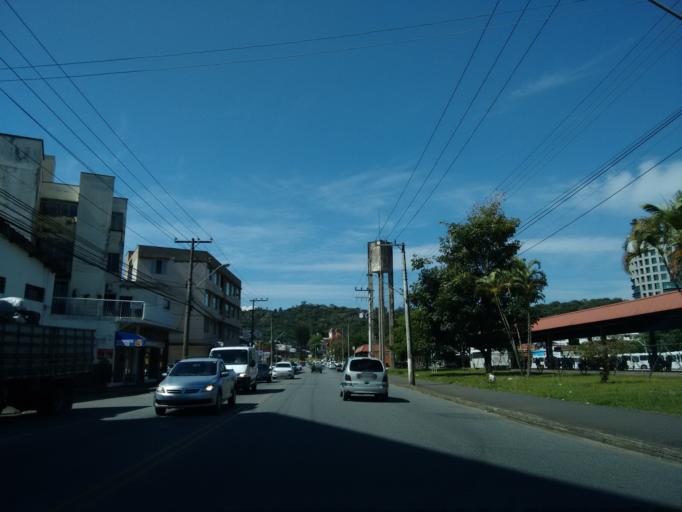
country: BR
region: Santa Catarina
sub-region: Blumenau
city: Blumenau
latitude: -26.9289
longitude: -49.0583
